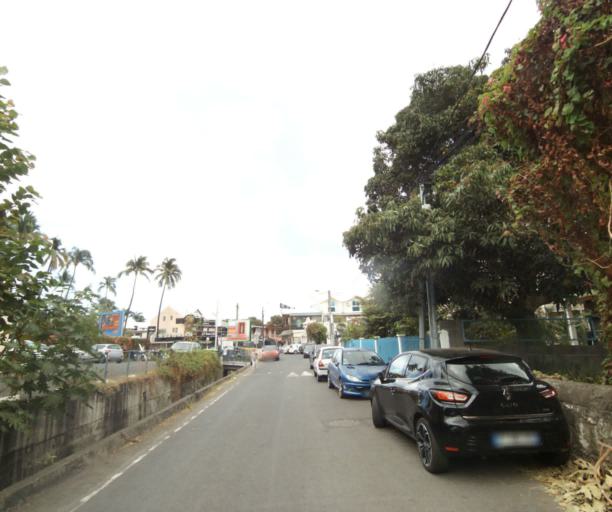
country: RE
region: Reunion
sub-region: Reunion
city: Saint-Paul
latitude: -21.0517
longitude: 55.2281
